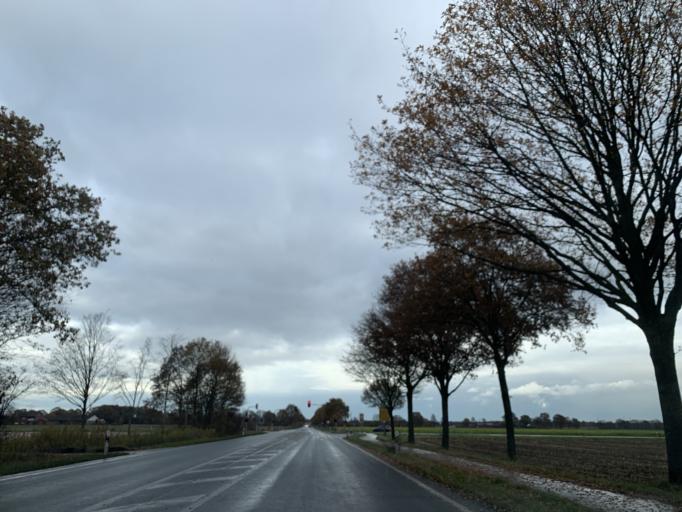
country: NL
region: Overijssel
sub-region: Gemeente Enschede
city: Enschede
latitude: 52.1444
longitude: 6.9368
